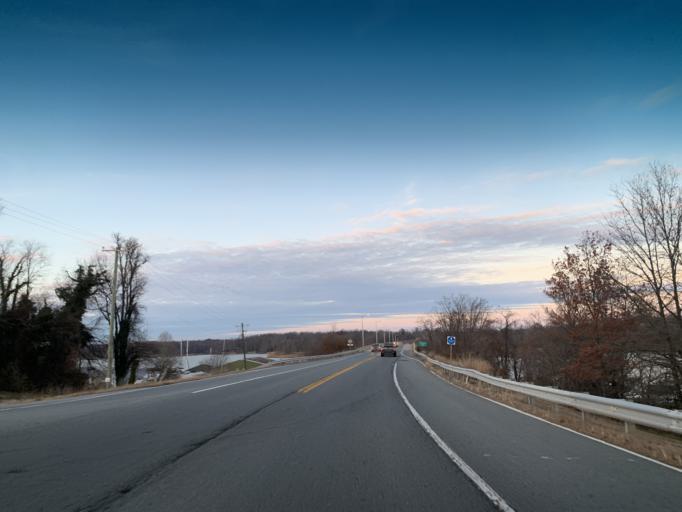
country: US
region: Maryland
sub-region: Cecil County
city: Elkton
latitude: 39.4585
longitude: -75.8715
